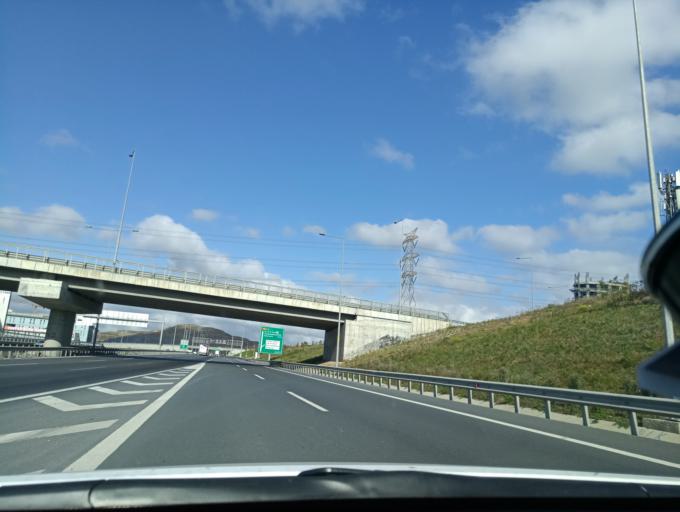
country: TR
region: Istanbul
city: Mahmutbey
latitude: 41.0662
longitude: 28.8143
